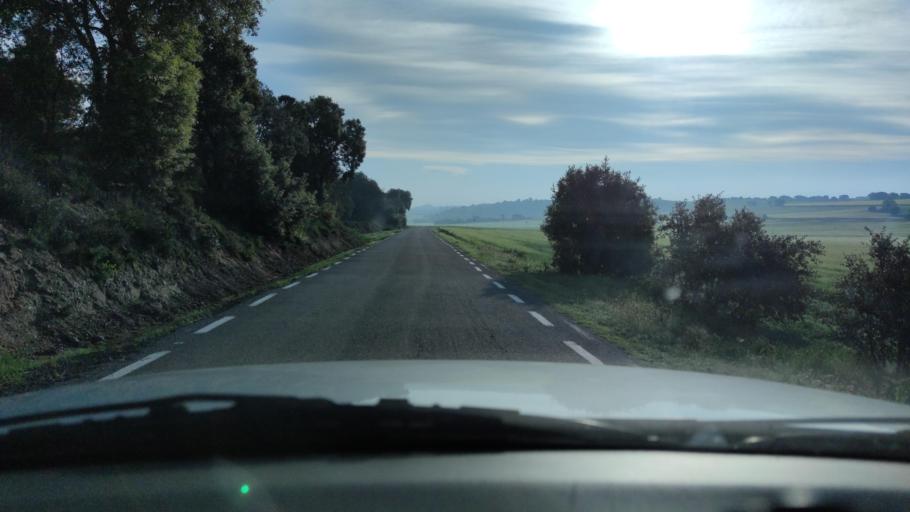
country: ES
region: Catalonia
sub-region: Provincia de Lleida
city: Artesa de Segre
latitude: 41.8572
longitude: 1.0604
